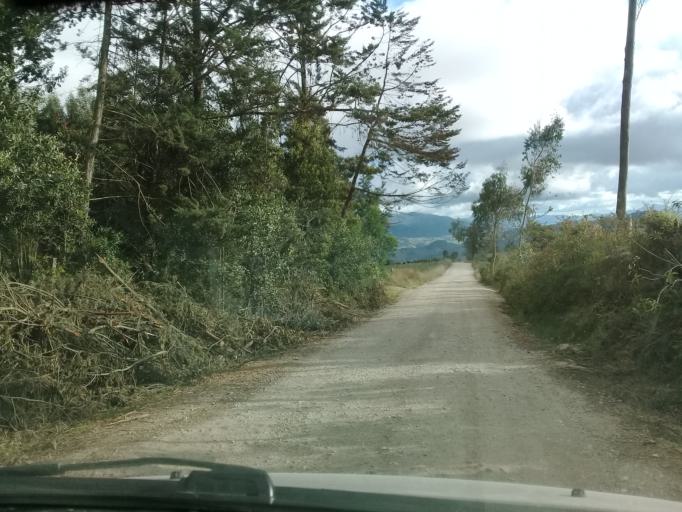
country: CO
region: Cundinamarca
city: Villapinzon
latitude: 5.2357
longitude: -73.6507
